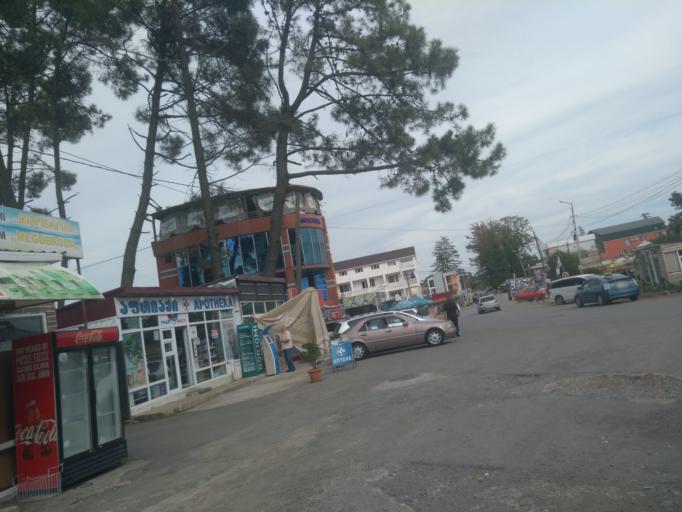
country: GE
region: Guria
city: Urek'i
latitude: 41.9979
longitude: 41.7598
